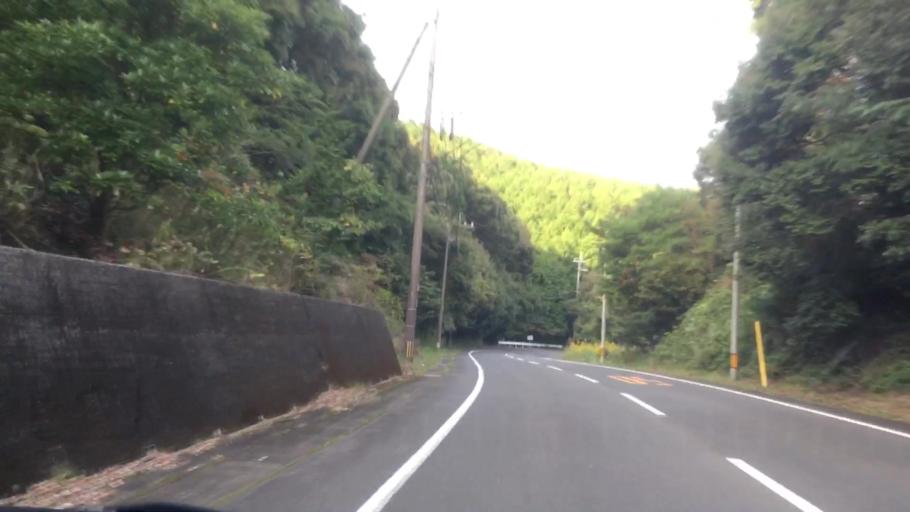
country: JP
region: Nagasaki
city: Sasebo
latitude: 32.9785
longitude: 129.7113
